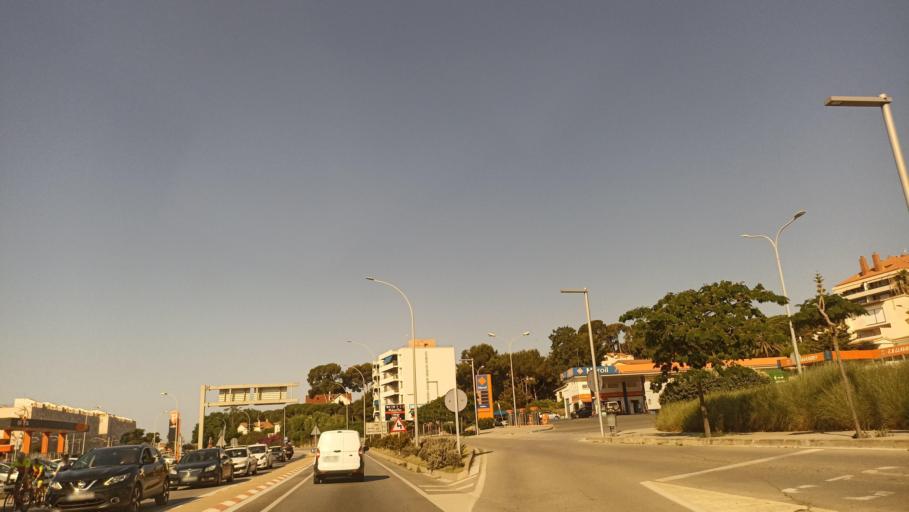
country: ES
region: Catalonia
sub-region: Provincia de Barcelona
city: Sant Andreu de Llavaneres
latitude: 41.5558
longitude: 2.4979
